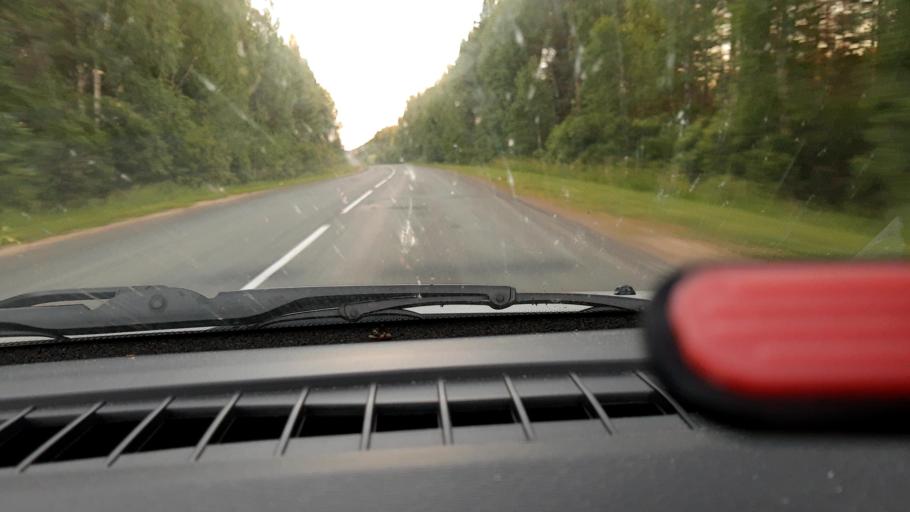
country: RU
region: Nizjnij Novgorod
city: Tonkino
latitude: 57.2992
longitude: 46.4627
